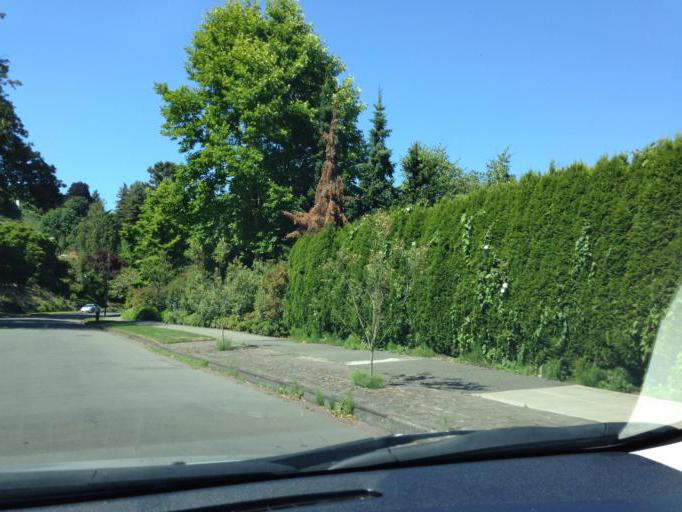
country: US
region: Washington
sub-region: King County
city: Seattle
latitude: 47.6226
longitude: -122.2839
